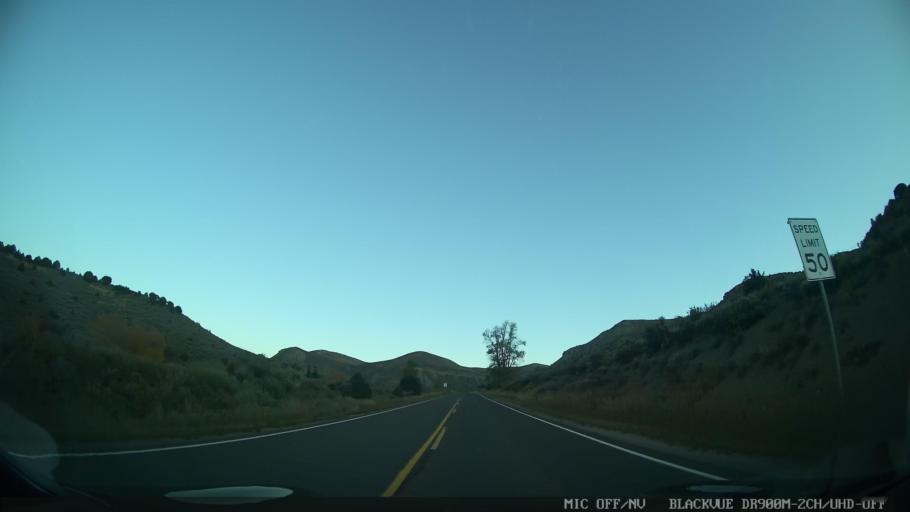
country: US
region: Colorado
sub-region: Eagle County
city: Edwards
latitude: 39.7649
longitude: -106.6781
